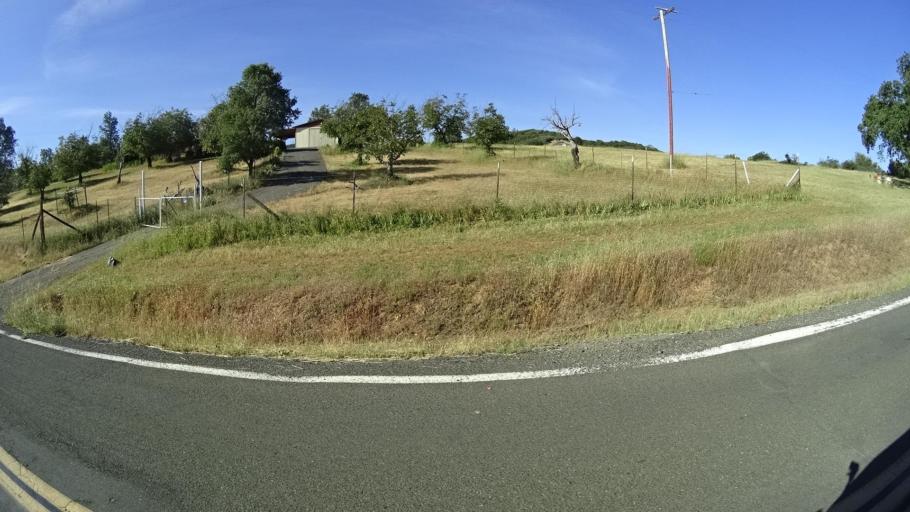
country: US
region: California
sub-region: Lake County
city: Lakeport
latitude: 39.0412
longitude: -122.9448
